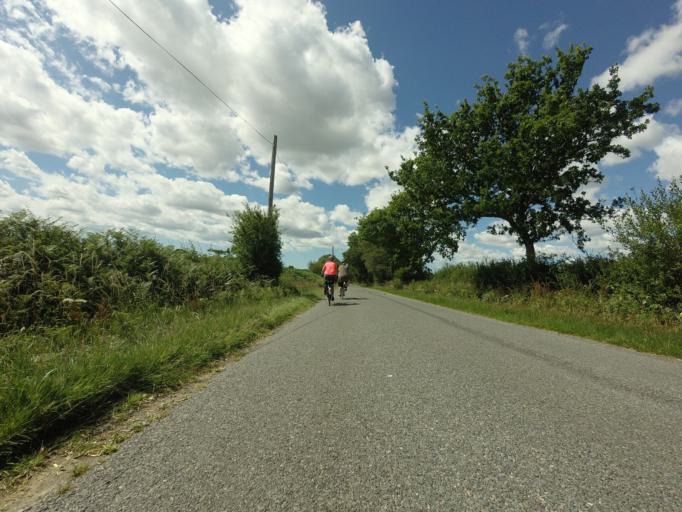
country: GB
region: England
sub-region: East Sussex
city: Hailsham
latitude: 50.8830
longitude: 0.1859
